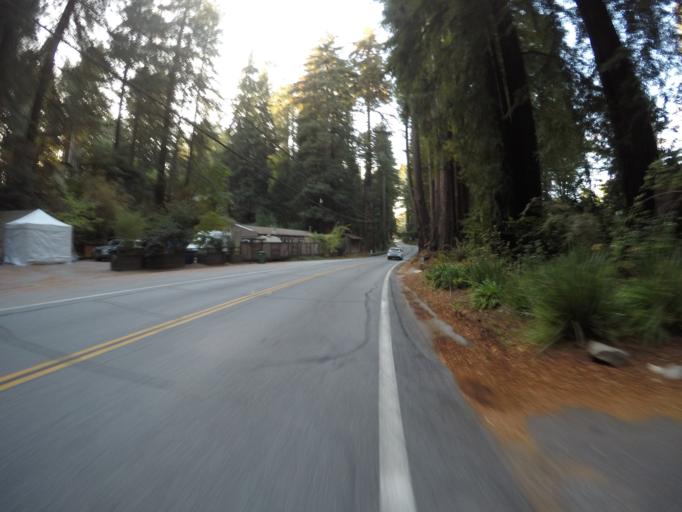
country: US
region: California
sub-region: Santa Cruz County
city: Felton
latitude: 37.0389
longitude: -122.0691
